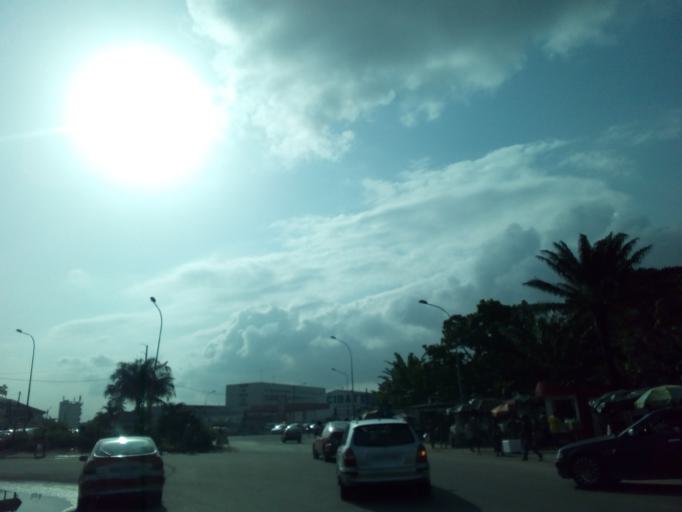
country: CI
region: Lagunes
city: Abidjan
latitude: 5.2949
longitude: -4.0037
